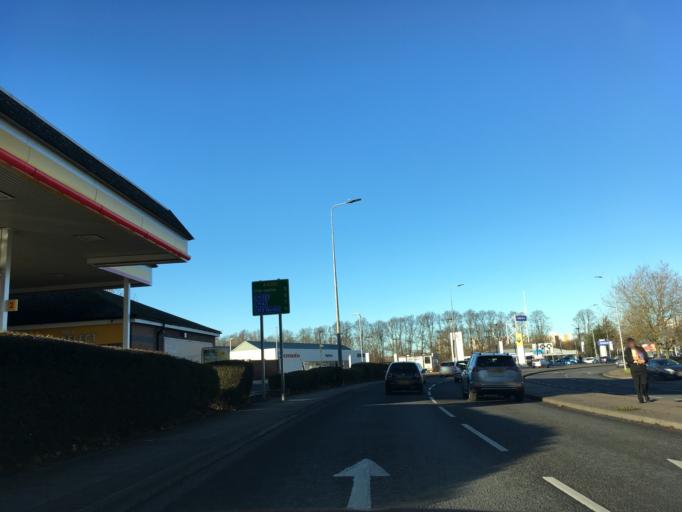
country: GB
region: England
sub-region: Bath and North East Somerset
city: Whitchurch
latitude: 51.4427
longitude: -2.5614
